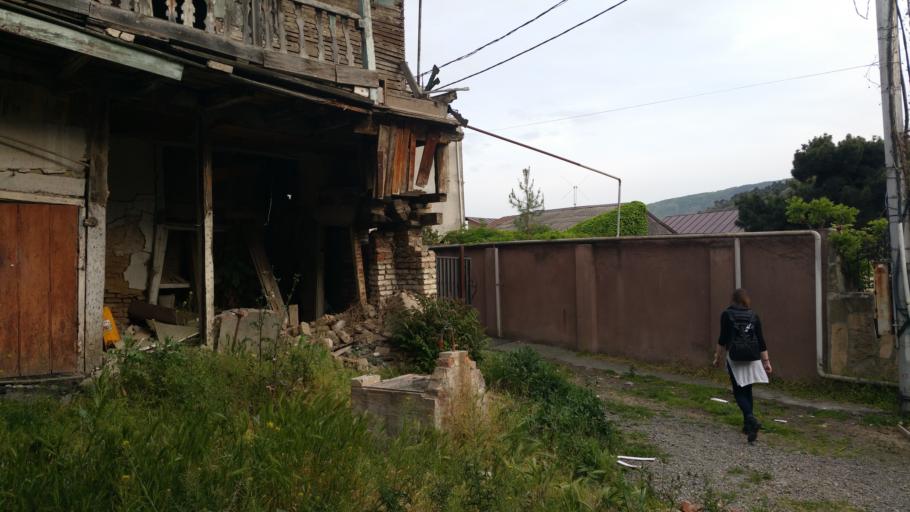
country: GE
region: T'bilisi
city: Tbilisi
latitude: 41.6908
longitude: 44.8141
